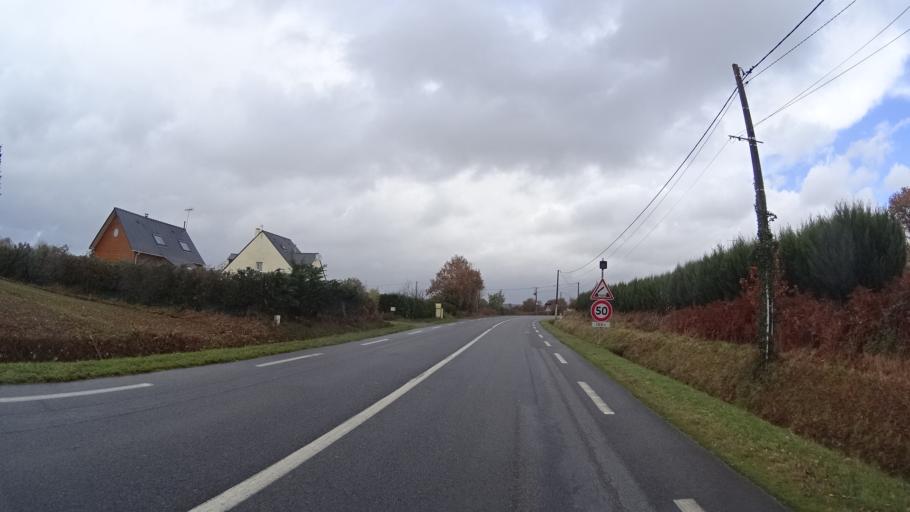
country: FR
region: Brittany
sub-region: Departement du Morbihan
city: Rieux
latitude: 47.5773
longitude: -2.1286
